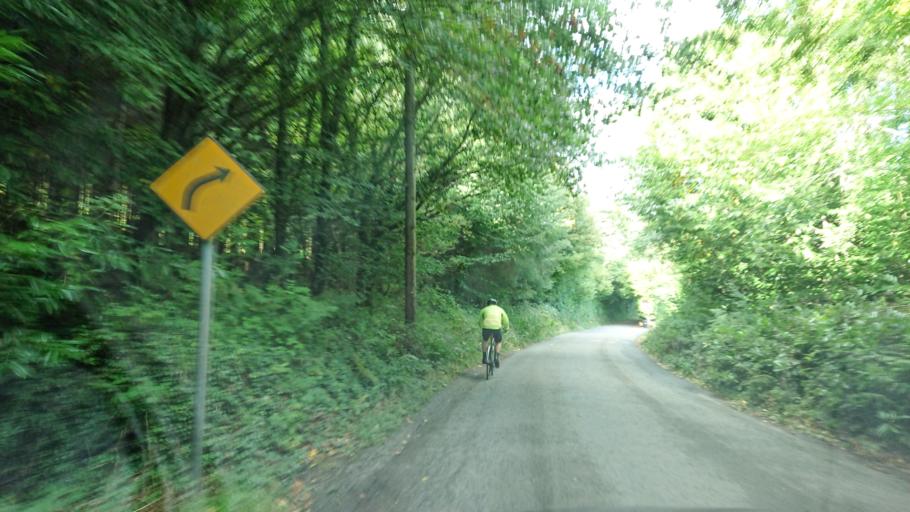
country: IE
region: Munster
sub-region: Waterford
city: Dungarvan
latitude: 52.1225
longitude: -7.6892
